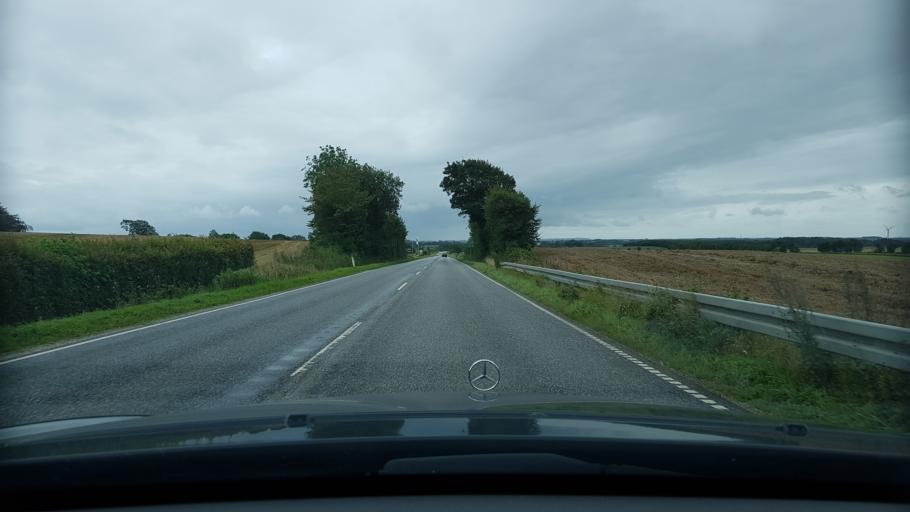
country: DK
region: Central Jutland
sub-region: Randers Kommune
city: Spentrup
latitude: 56.5558
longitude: 10.1051
